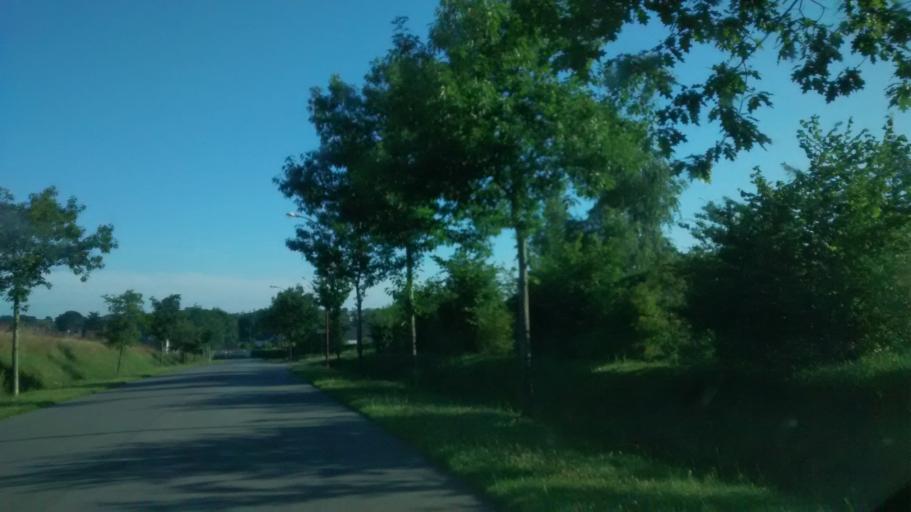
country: FR
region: Brittany
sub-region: Departement du Morbihan
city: Campeneac
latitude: 47.9523
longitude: -2.2893
